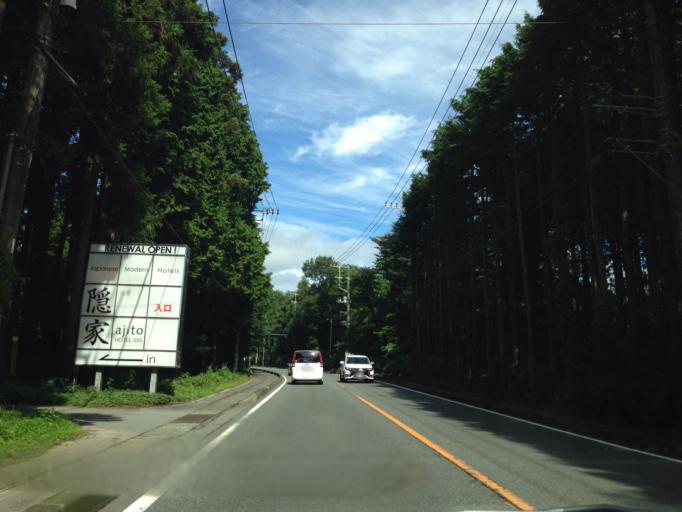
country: JP
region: Shizuoka
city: Gotemba
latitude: 35.3326
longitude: 138.9002
